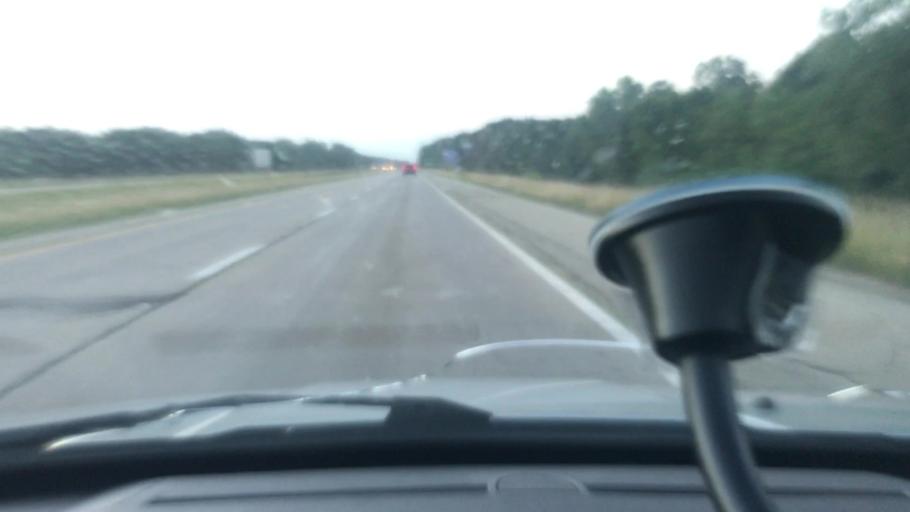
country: US
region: Illinois
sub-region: Peoria County
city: Bellevue
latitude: 40.7605
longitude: -89.6707
